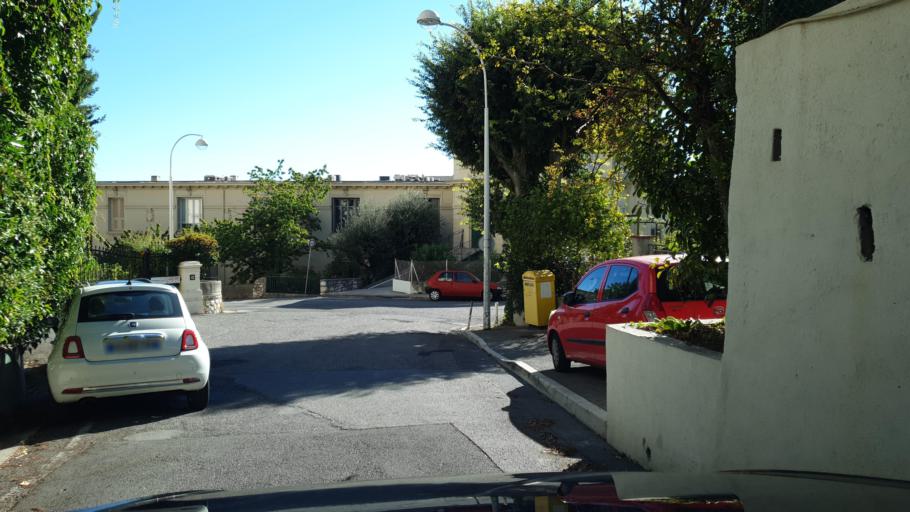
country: FR
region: Provence-Alpes-Cote d'Azur
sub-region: Departement des Alpes-Maritimes
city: Nice
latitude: 43.7058
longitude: 7.2761
